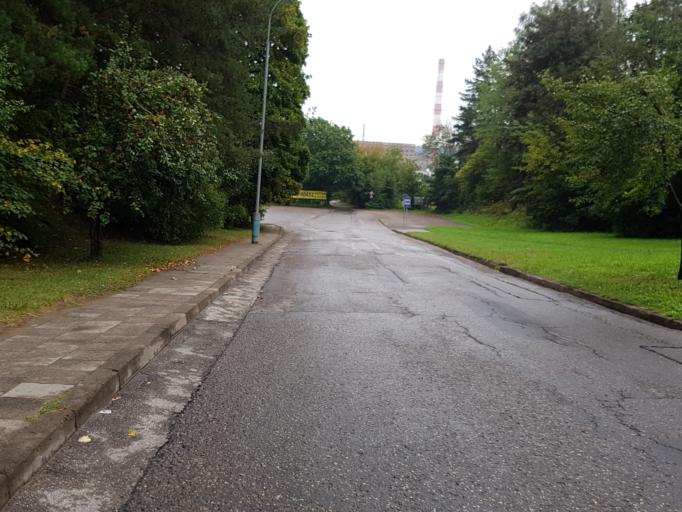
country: LT
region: Vilnius County
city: Lazdynai
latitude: 54.6671
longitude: 25.2200
